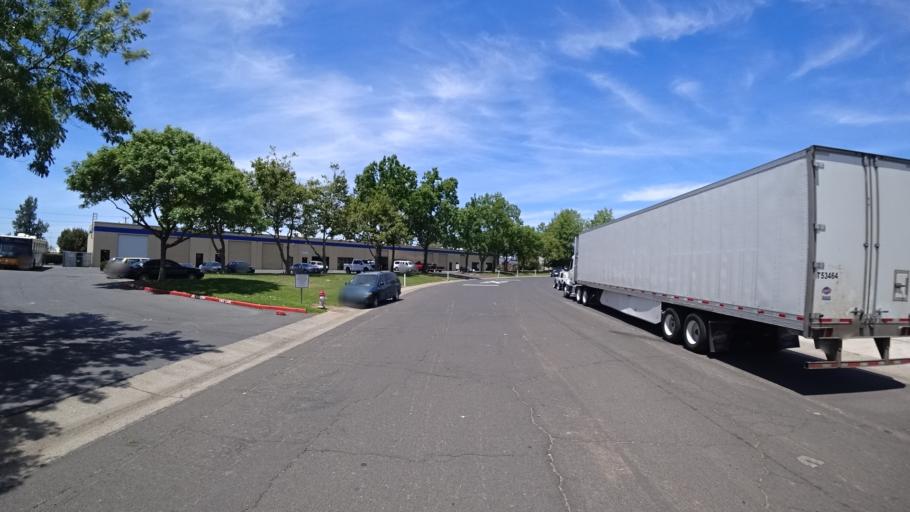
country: US
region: California
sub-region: Sacramento County
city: Rosemont
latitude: 38.5308
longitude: -121.3888
